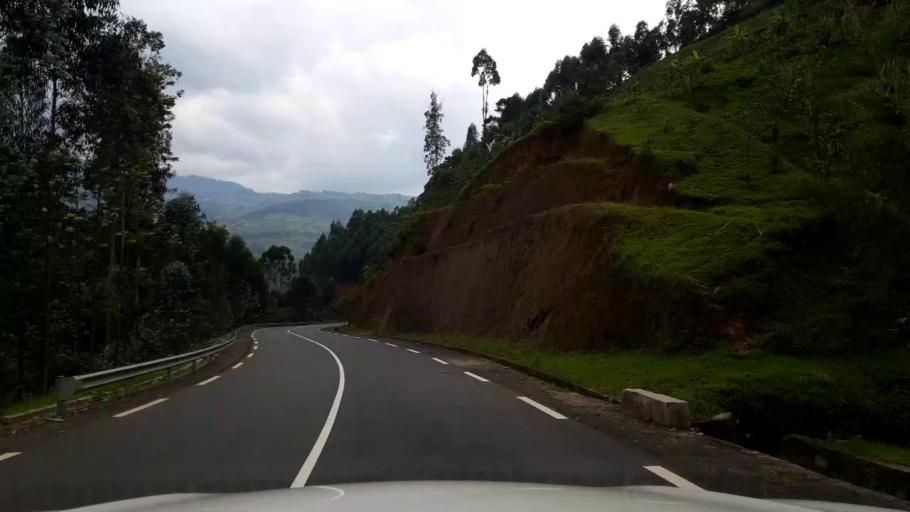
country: RW
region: Western Province
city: Kibuye
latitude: -1.9083
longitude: 29.3630
